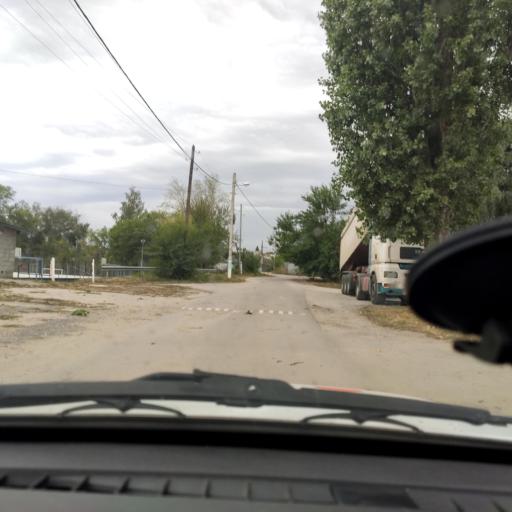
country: RU
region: Voronezj
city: Strelitsa
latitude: 51.6064
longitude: 38.9059
